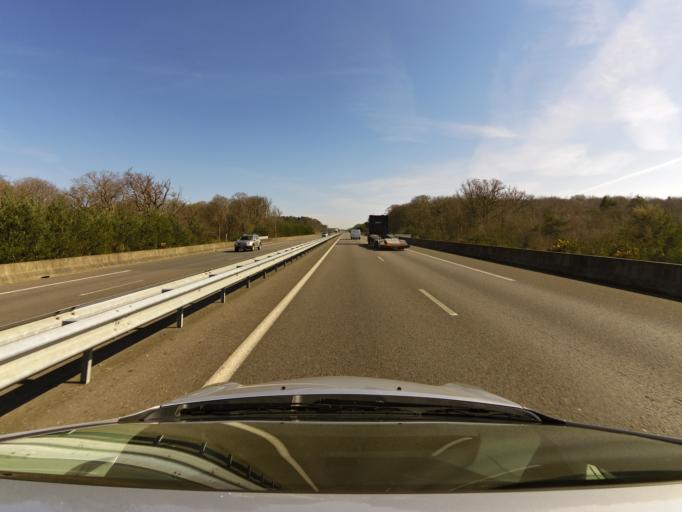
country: FR
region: Brittany
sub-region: Departement d'Ille-et-Vilaine
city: Fouillard
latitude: 48.1745
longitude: -1.5658
